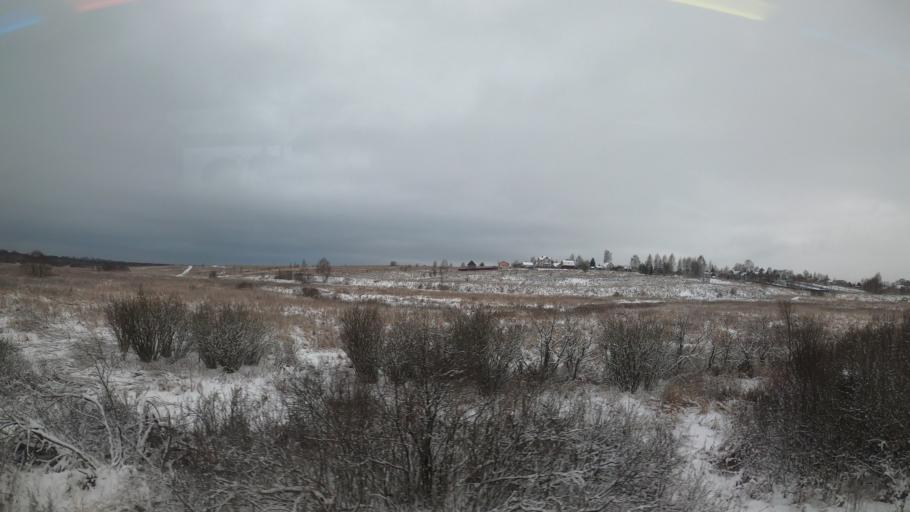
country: RU
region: Jaroslavl
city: Pereslavl'-Zalesskiy
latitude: 56.7001
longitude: 38.9140
